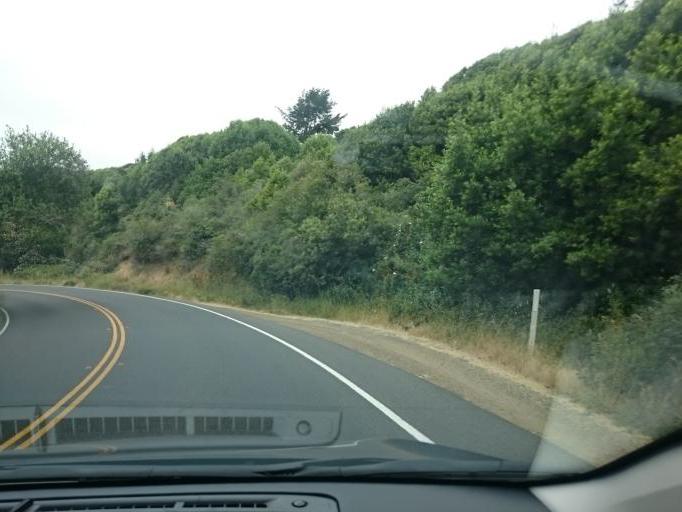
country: US
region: California
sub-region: Marin County
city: Inverness
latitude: 38.1032
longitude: -122.8369
